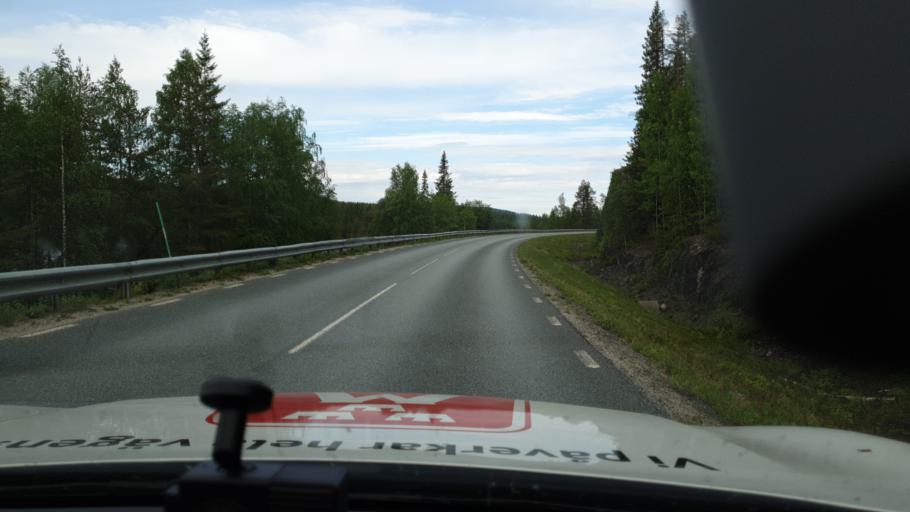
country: SE
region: Vaesterbotten
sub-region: Lycksele Kommun
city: Soderfors
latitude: 65.0795
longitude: 18.3350
